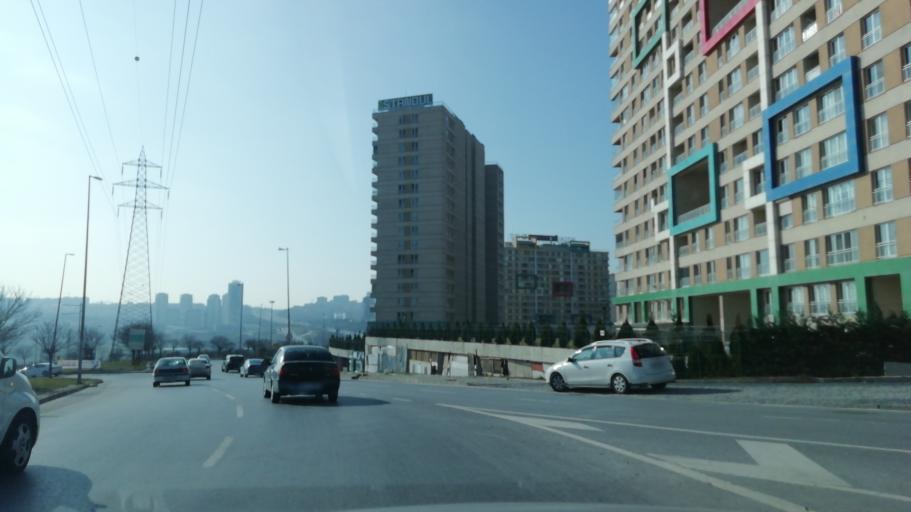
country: TR
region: Istanbul
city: Esenyurt
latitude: 41.0600
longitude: 28.7101
